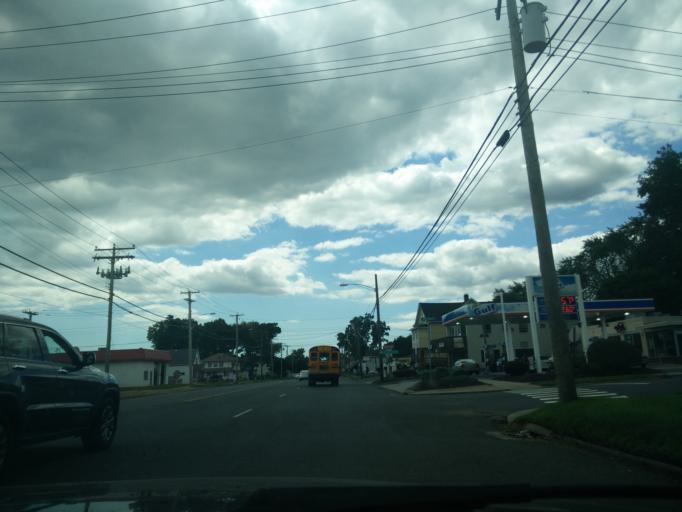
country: US
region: Connecticut
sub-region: New Haven County
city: New Haven
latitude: 41.3569
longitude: -72.9275
